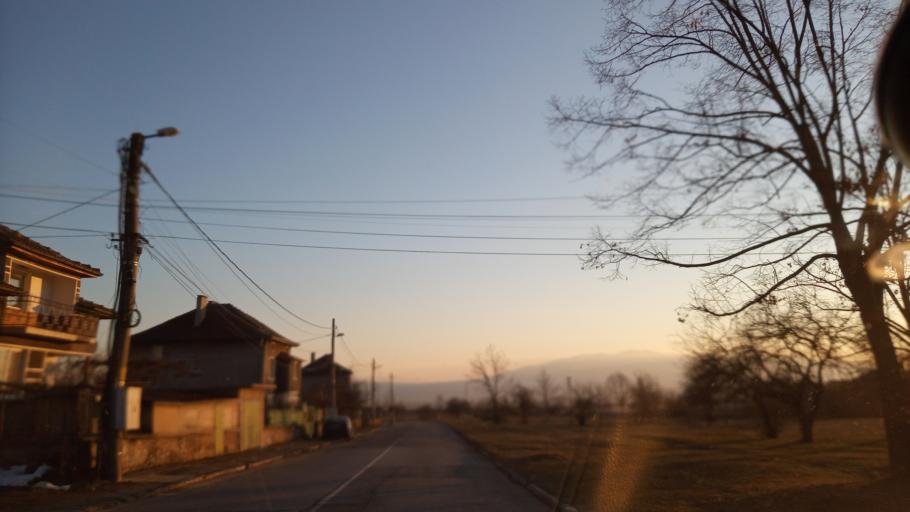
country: BG
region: Sofia-Capital
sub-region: Stolichna Obshtina
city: Bukhovo
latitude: 42.7828
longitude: 23.5186
